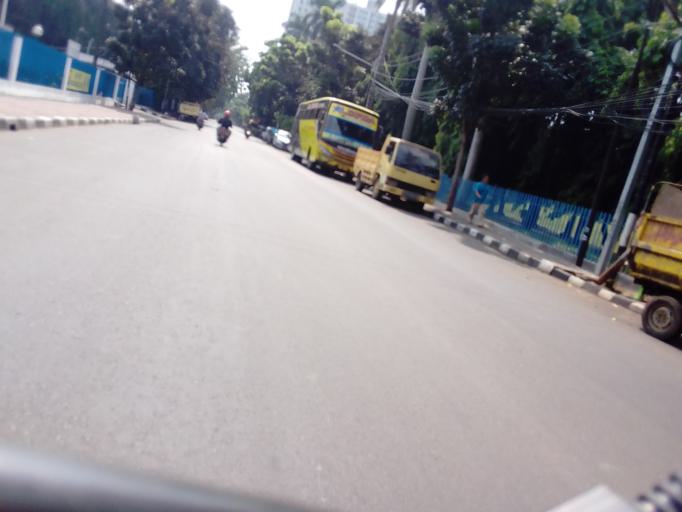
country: ID
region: Jakarta Raya
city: Jakarta
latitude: -6.2046
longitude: 106.8092
